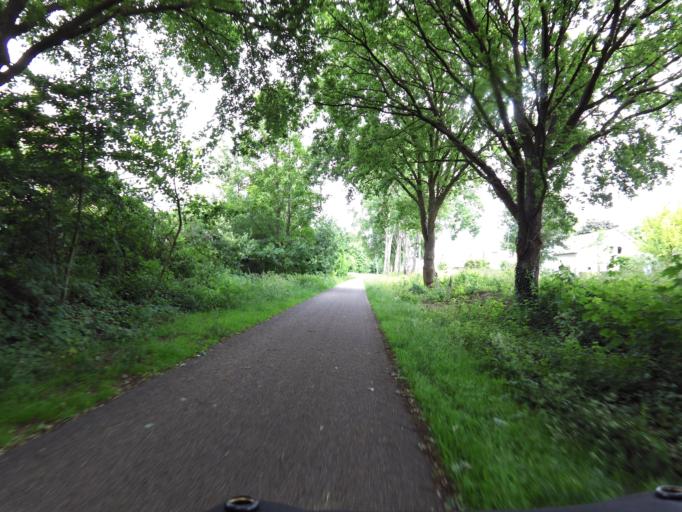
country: NL
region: North Brabant
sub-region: Gemeente Baarle-Nassau
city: Baarle-Nassau
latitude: 51.4501
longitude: 4.9269
